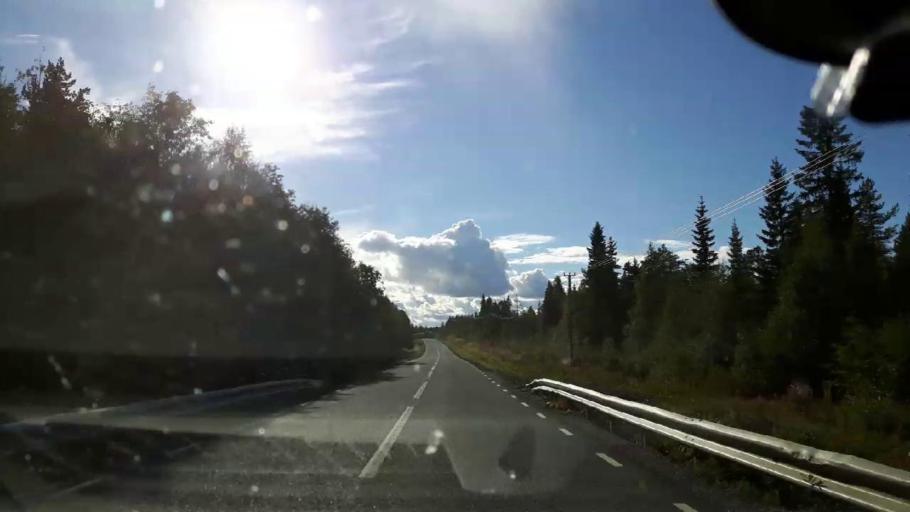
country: SE
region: Jaemtland
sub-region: Stroemsunds Kommun
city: Stroemsund
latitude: 63.5759
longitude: 15.6404
